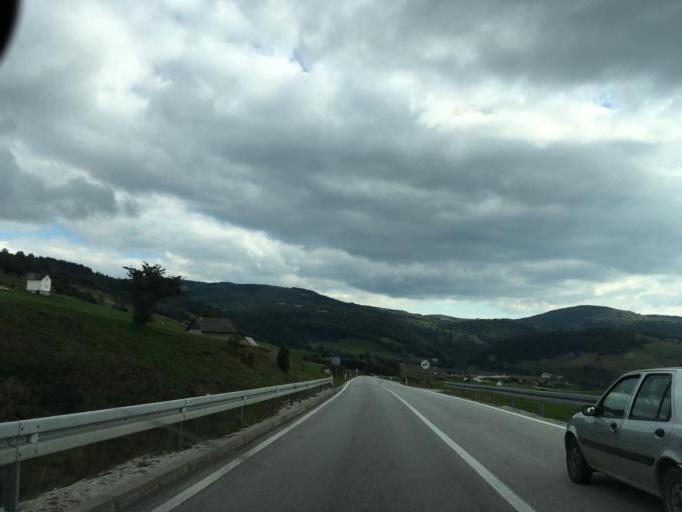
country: BA
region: Federation of Bosnia and Herzegovina
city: Novi Travnik
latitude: 44.1113
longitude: 17.5750
